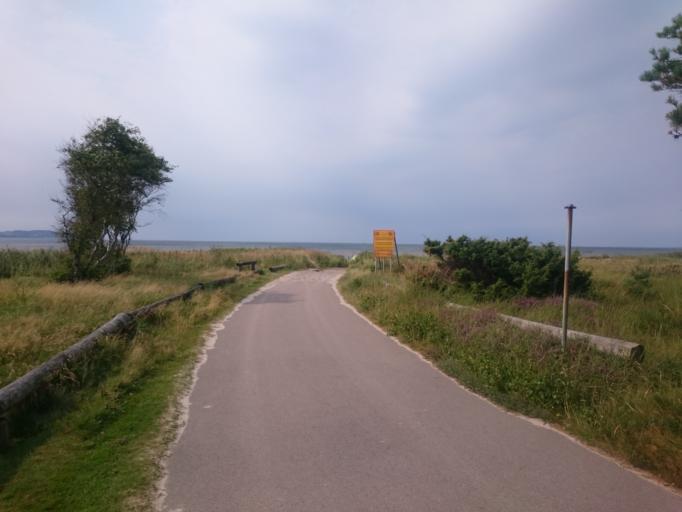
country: SE
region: Halland
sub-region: Laholms Kommun
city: Mellbystrand
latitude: 56.4595
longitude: 12.9134
